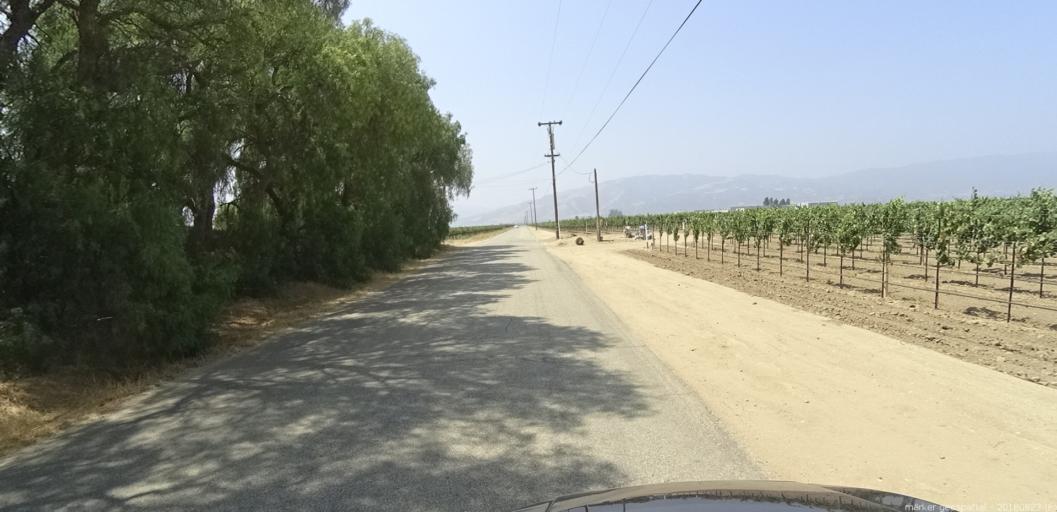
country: US
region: California
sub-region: Monterey County
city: Greenfield
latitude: 36.3279
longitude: -121.2623
